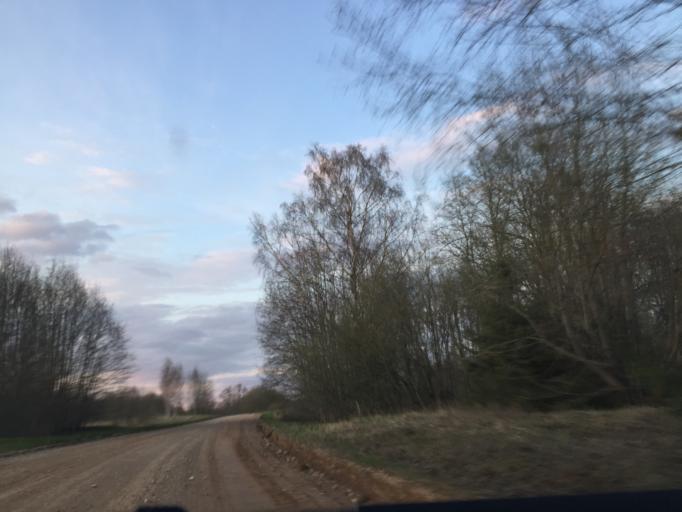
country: LV
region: Aluksnes Rajons
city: Aluksne
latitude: 57.3454
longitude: 26.9674
